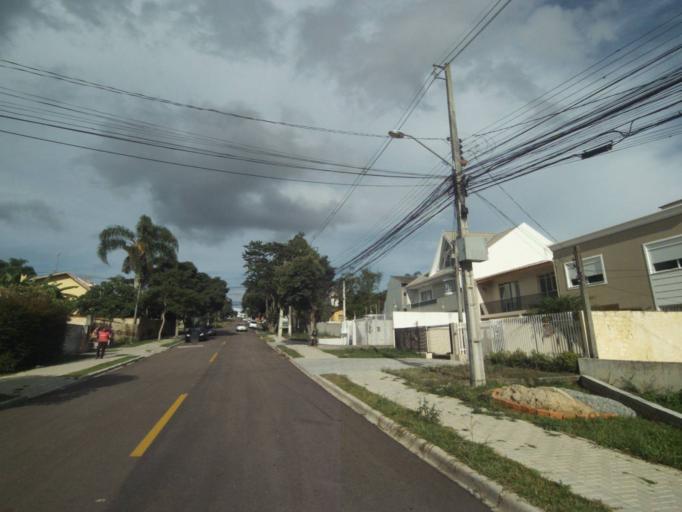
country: BR
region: Parana
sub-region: Curitiba
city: Curitiba
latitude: -25.4431
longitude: -49.3129
